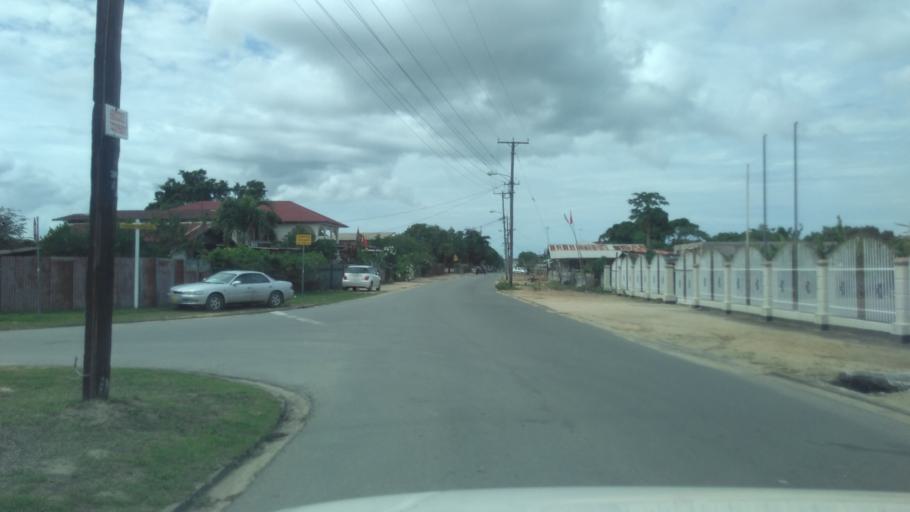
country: SR
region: Paramaribo
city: Paramaribo
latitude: 5.8490
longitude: -55.1273
